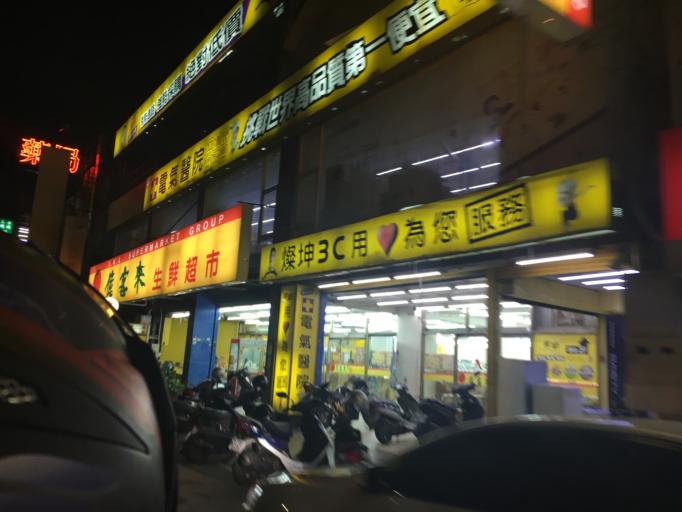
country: TW
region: Taiwan
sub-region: Hsinchu
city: Hsinchu
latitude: 24.7952
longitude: 120.9732
